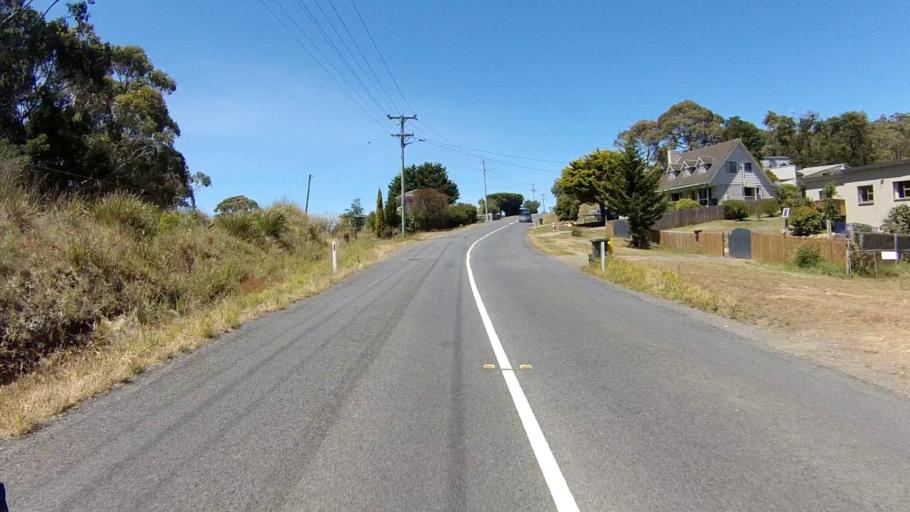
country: AU
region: Tasmania
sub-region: Clarence
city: Howrah
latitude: -42.8590
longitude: 147.4150
